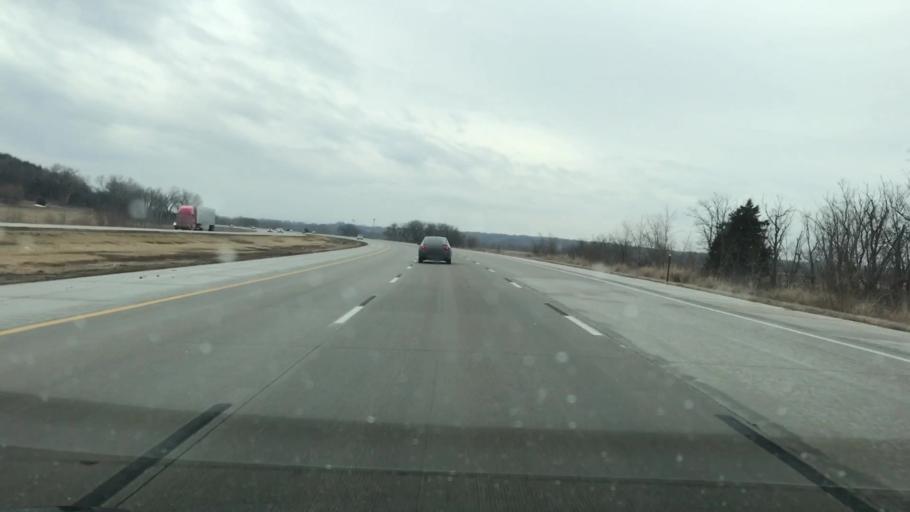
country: US
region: Nebraska
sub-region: Saunders County
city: Ashland
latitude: 41.0597
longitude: -96.2944
